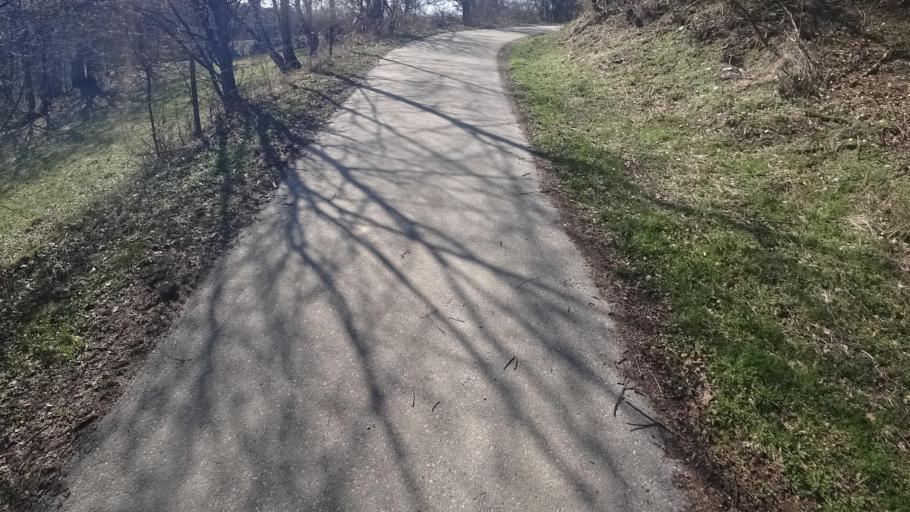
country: DE
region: Rheinland-Pfalz
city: Tiefenbach
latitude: 49.9547
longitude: 7.5601
